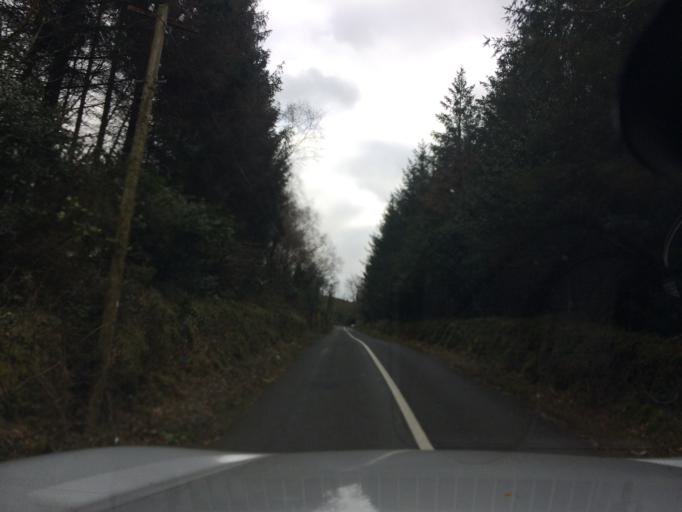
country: IE
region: Munster
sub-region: South Tipperary
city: Cluain Meala
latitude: 52.3451
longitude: -7.6378
